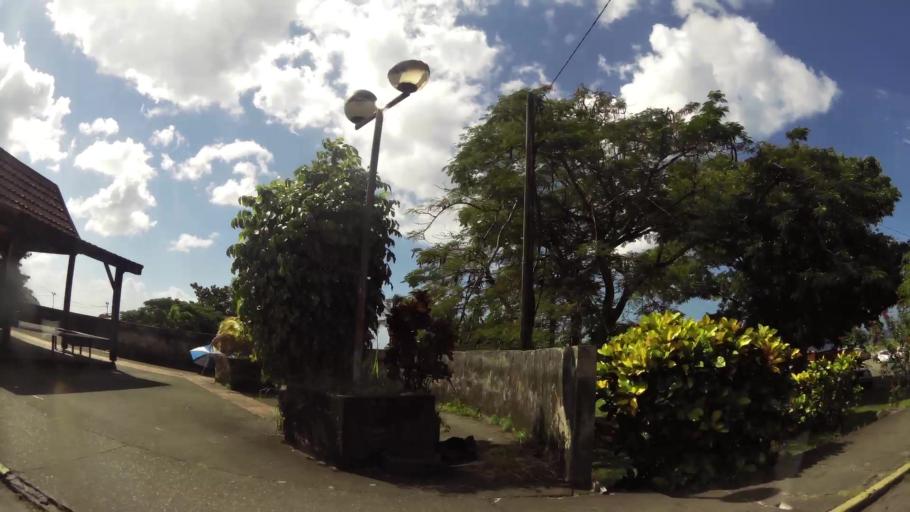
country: MQ
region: Martinique
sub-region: Martinique
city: Saint-Pierre
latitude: 14.7486
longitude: -61.1786
